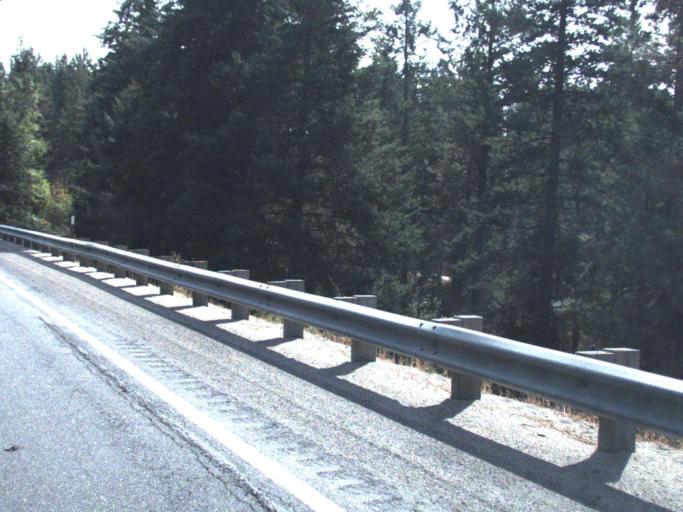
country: US
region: Washington
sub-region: Spokane County
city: Deer Park
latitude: 48.0311
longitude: -117.6025
